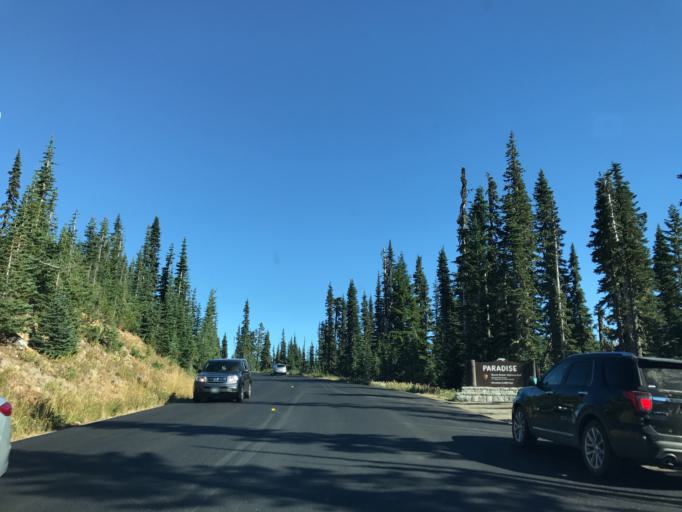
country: US
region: Washington
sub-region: Pierce County
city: Buckley
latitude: 46.7819
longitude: -121.7476
